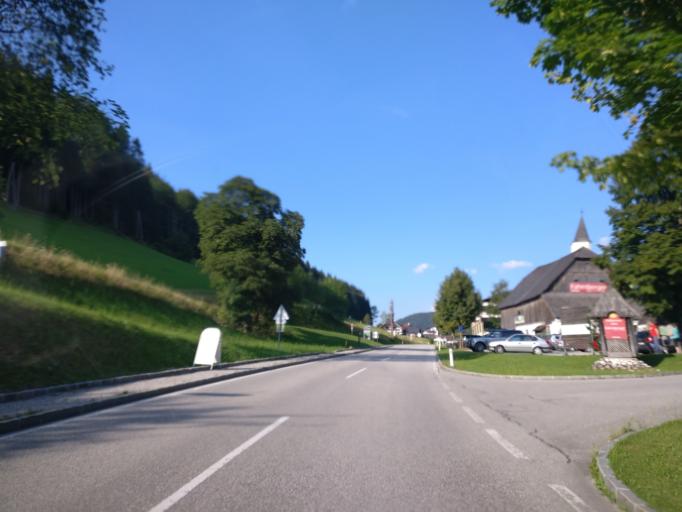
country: AT
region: Lower Austria
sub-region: Politischer Bezirk Scheibbs
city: Gostling an der Ybbs
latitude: 47.7432
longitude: 14.8920
